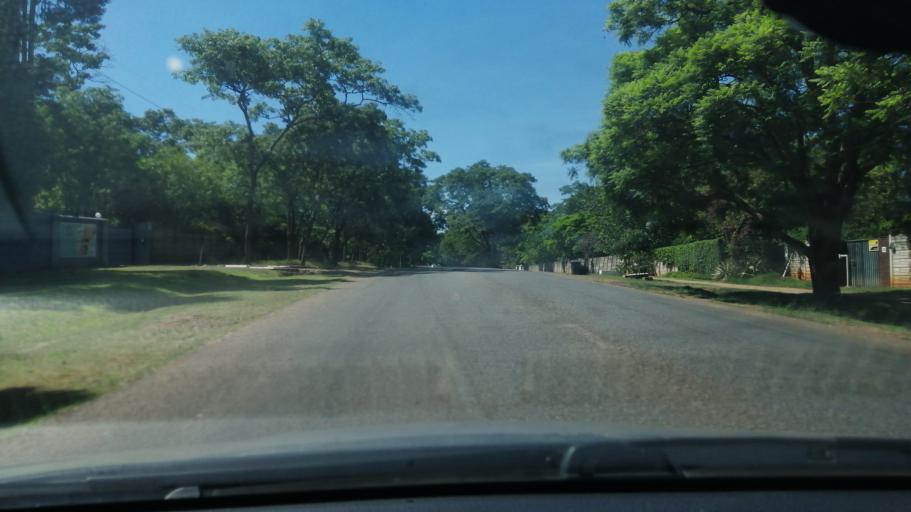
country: ZW
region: Harare
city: Harare
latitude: -17.7999
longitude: 31.1288
